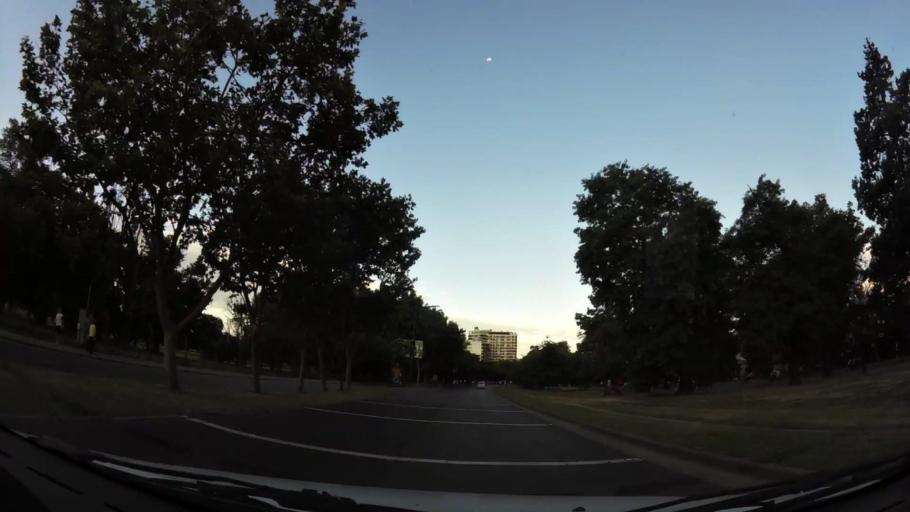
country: AR
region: Buenos Aires
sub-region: Partido de San Isidro
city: San Isidro
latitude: -34.4817
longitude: -58.5105
